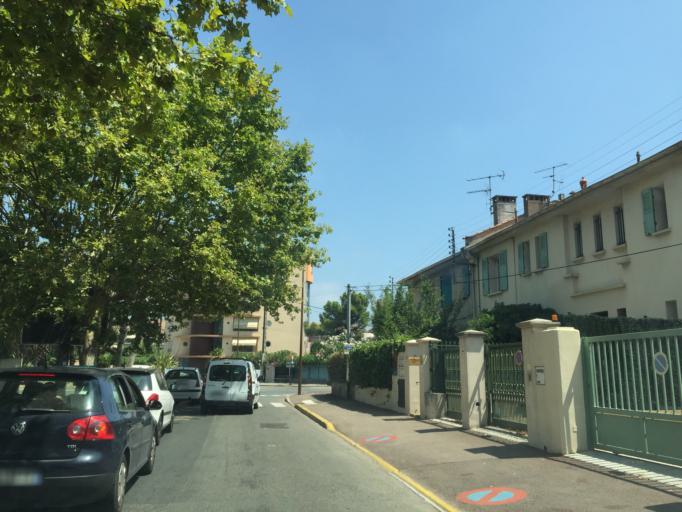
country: FR
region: Provence-Alpes-Cote d'Azur
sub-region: Departement du Var
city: Saint-Raphael
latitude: 43.4259
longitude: 6.7618
